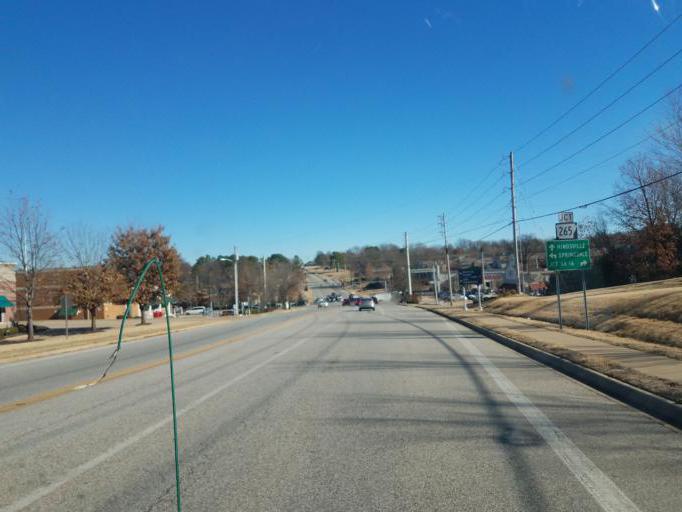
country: US
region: Arkansas
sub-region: Washington County
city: Fayetteville
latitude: 36.0873
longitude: -94.1233
